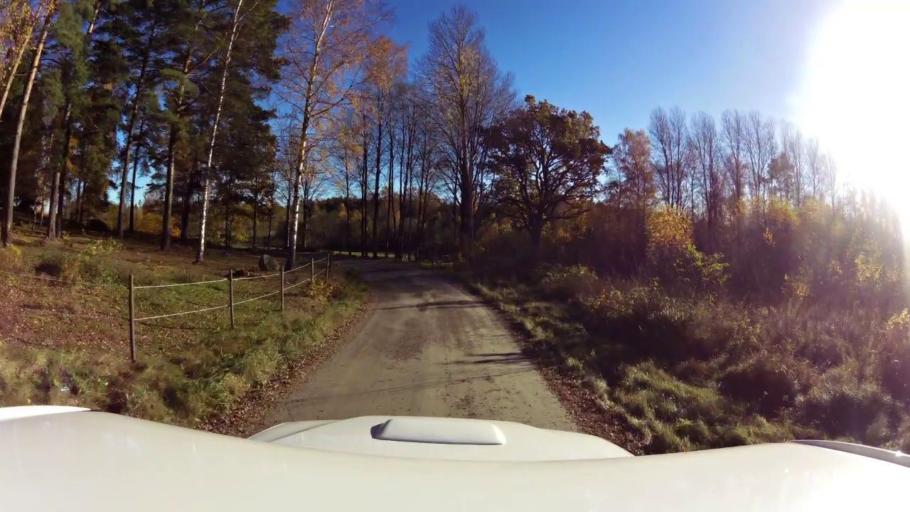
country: SE
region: OEstergoetland
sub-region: Linkopings Kommun
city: Ljungsbro
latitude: 58.5257
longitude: 15.4906
